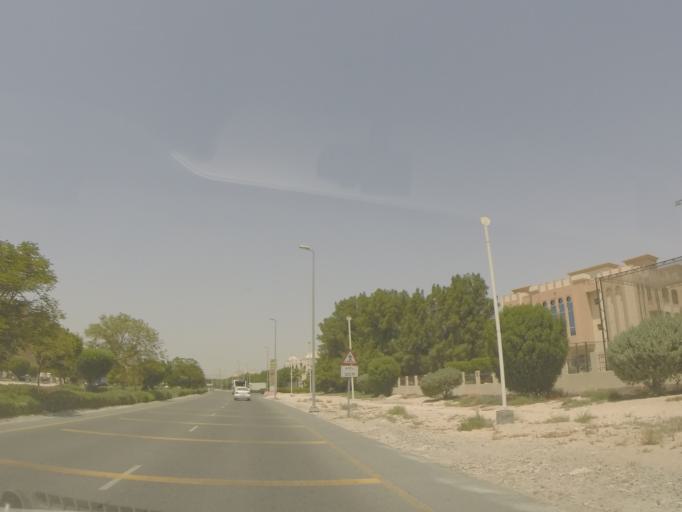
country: AE
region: Dubai
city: Dubai
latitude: 24.9936
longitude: 55.1793
